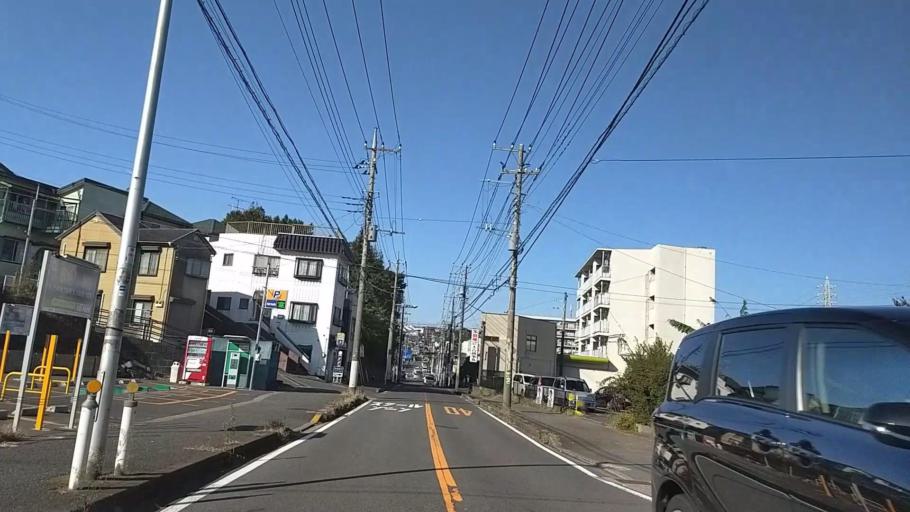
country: JP
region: Kanagawa
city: Yokohama
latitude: 35.4633
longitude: 139.5661
